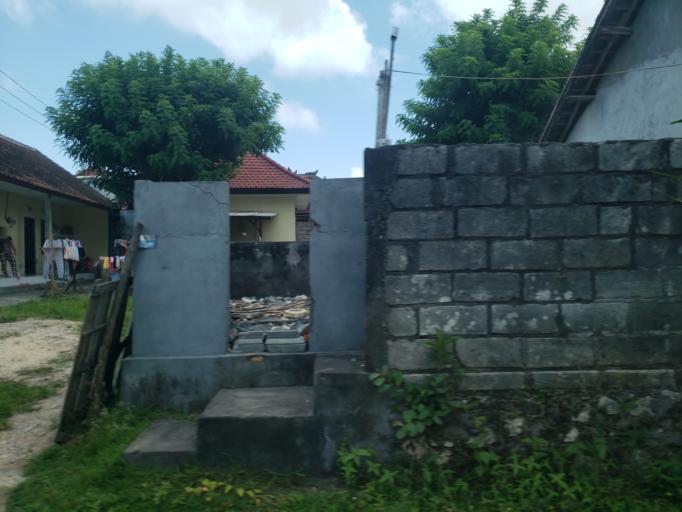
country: ID
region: Bali
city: Kangin
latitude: -8.8370
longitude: 115.1519
